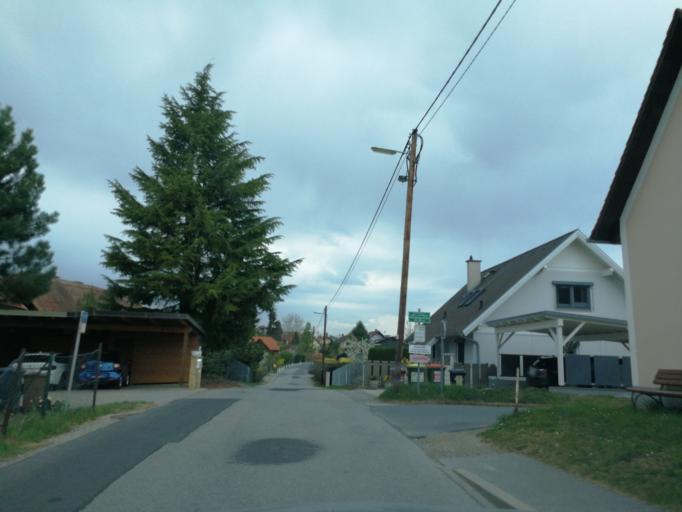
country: AT
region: Styria
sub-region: Politischer Bezirk Graz-Umgebung
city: Hart bei Graz
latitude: 47.0626
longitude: 15.5044
